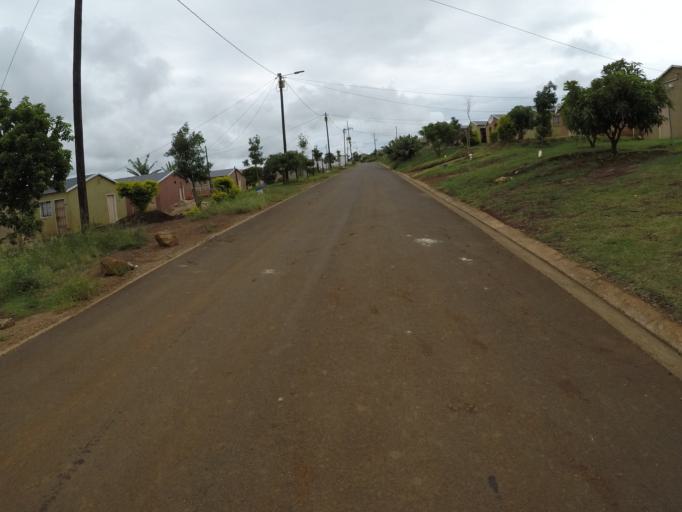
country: ZA
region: KwaZulu-Natal
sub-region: uThungulu District Municipality
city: Empangeni
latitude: -28.7596
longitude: 31.8750
